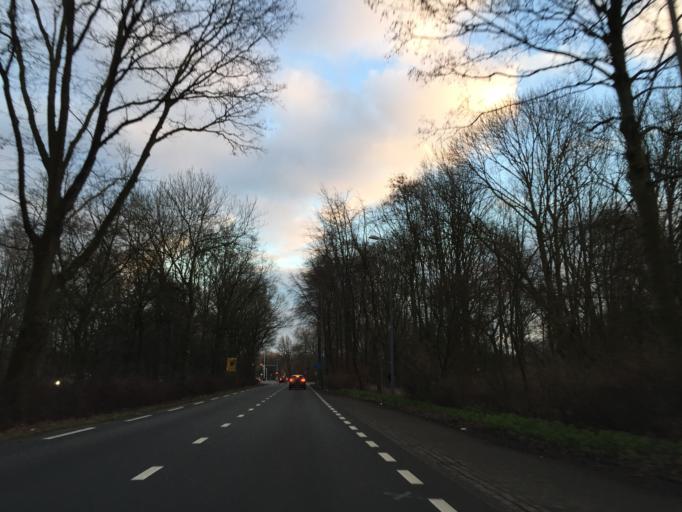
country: NL
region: South Holland
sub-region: Gemeente Rotterdam
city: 's-Gravenland
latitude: 51.9459
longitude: 4.5237
